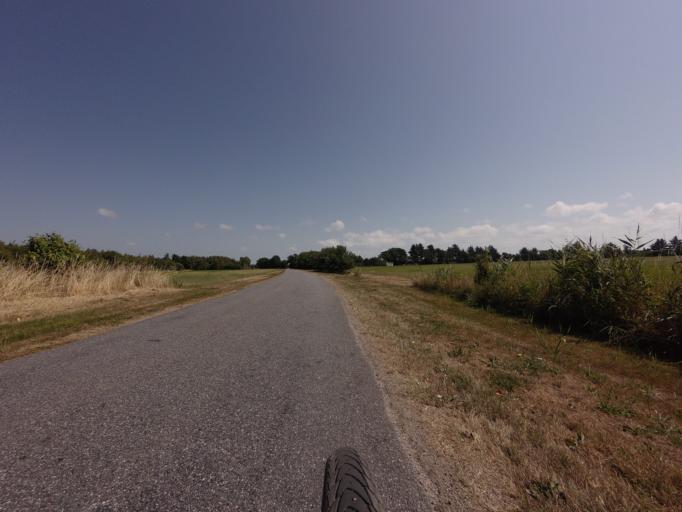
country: DK
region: North Denmark
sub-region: Laeso Kommune
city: Byrum
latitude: 57.2526
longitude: 10.9536
